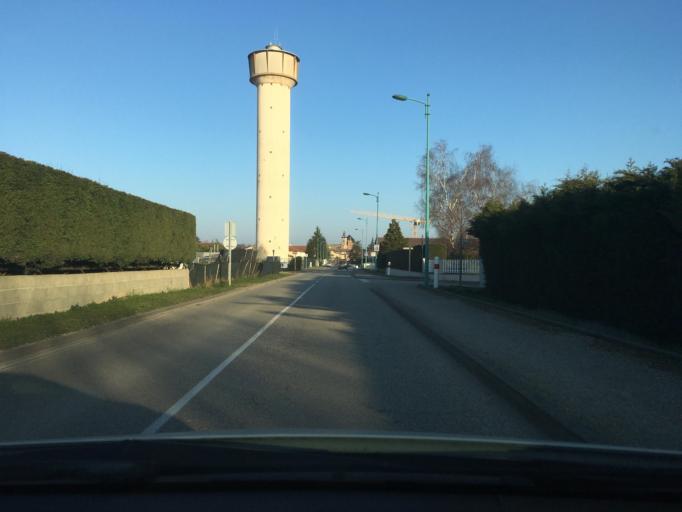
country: FR
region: Rhone-Alpes
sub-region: Departement de l'Ain
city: Amberieux-en-Dombes
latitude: 45.9925
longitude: 4.9087
